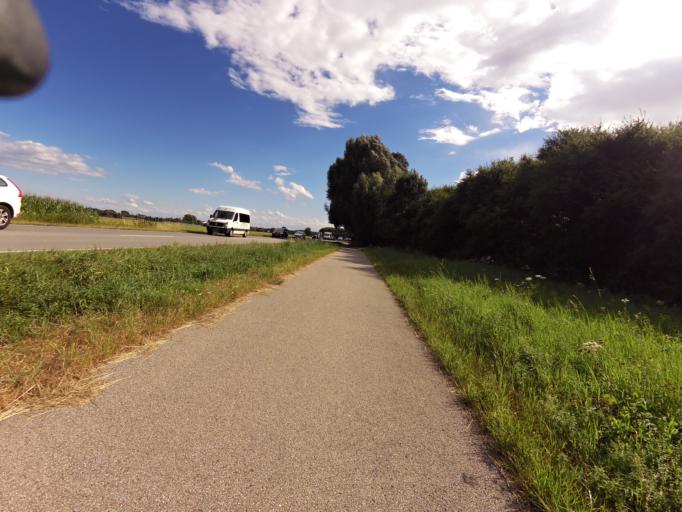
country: DE
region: Bavaria
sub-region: Upper Bavaria
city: Hallbergmoos
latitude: 48.3439
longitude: 11.7350
